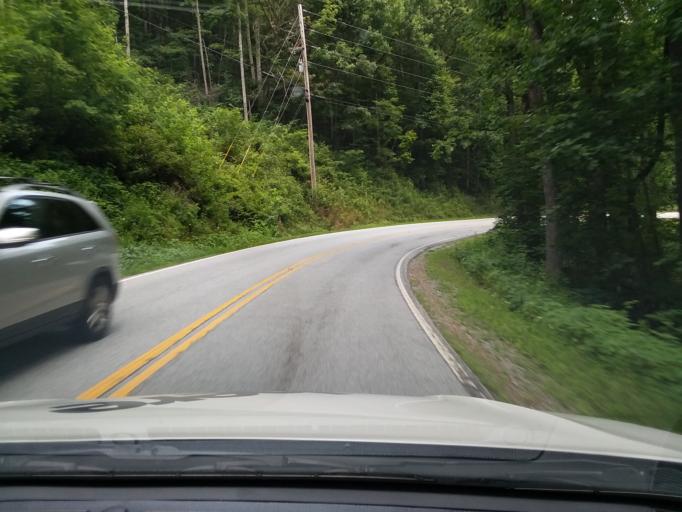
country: US
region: Georgia
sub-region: Rabun County
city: Mountain City
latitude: 35.0284
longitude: -83.2894
